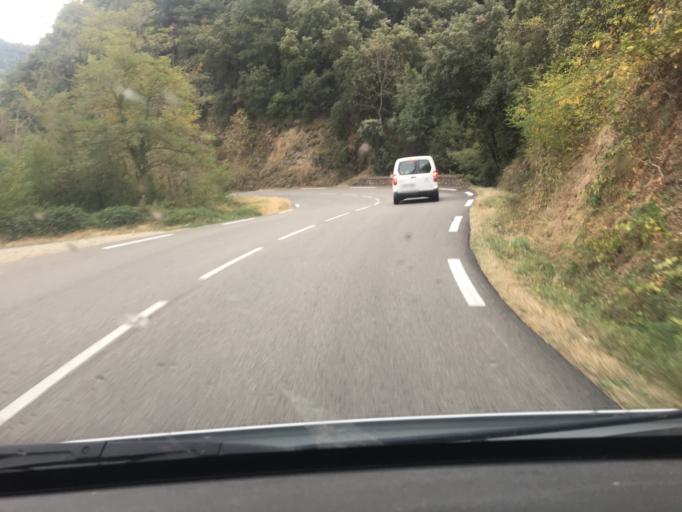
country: FR
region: Rhone-Alpes
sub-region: Departement de l'Ardeche
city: Saint-Jean-de-Muzols
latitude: 45.0583
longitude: 4.7790
